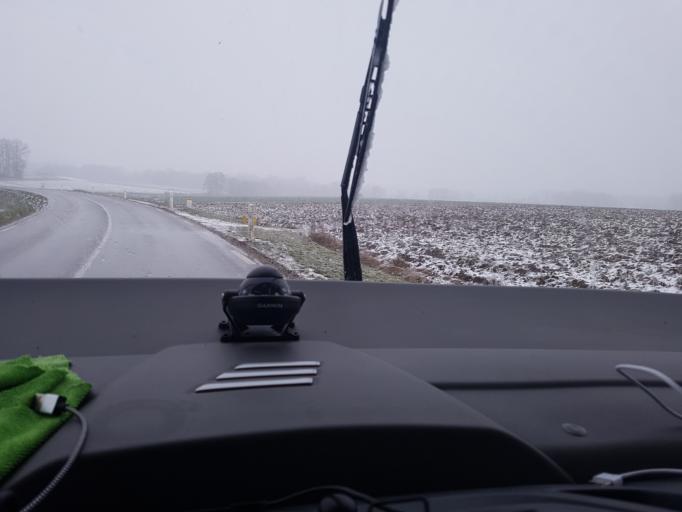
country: FR
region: Lorraine
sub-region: Departement de Meurthe-et-Moselle
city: Baccarat
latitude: 48.4945
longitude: 6.7889
